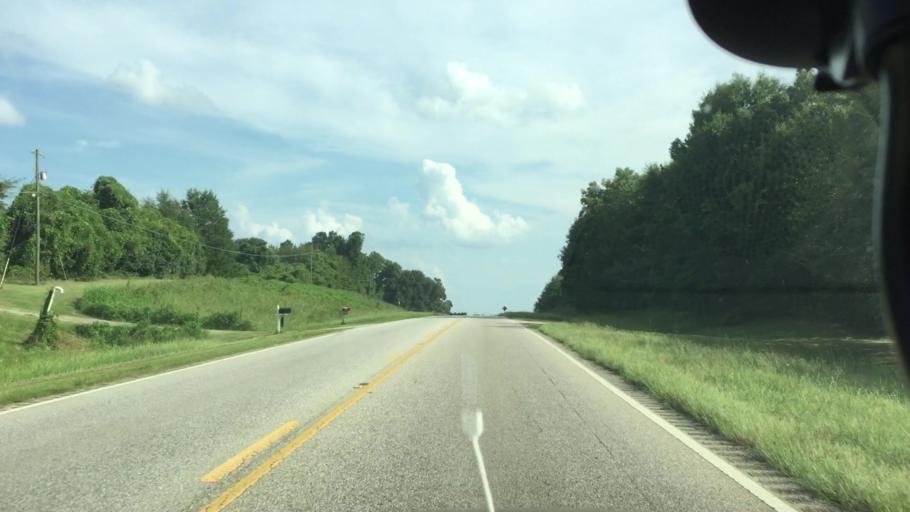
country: US
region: Alabama
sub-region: Pike County
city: Troy
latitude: 31.7144
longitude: -85.9594
